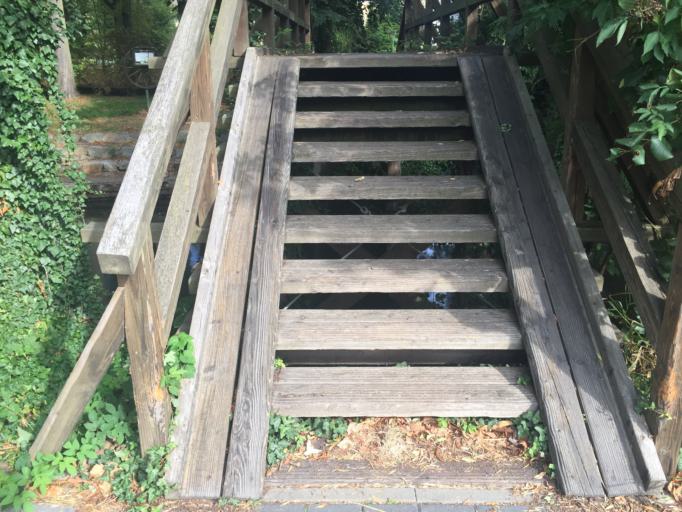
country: DE
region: Brandenburg
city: Burg
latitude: 51.8433
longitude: 14.1111
